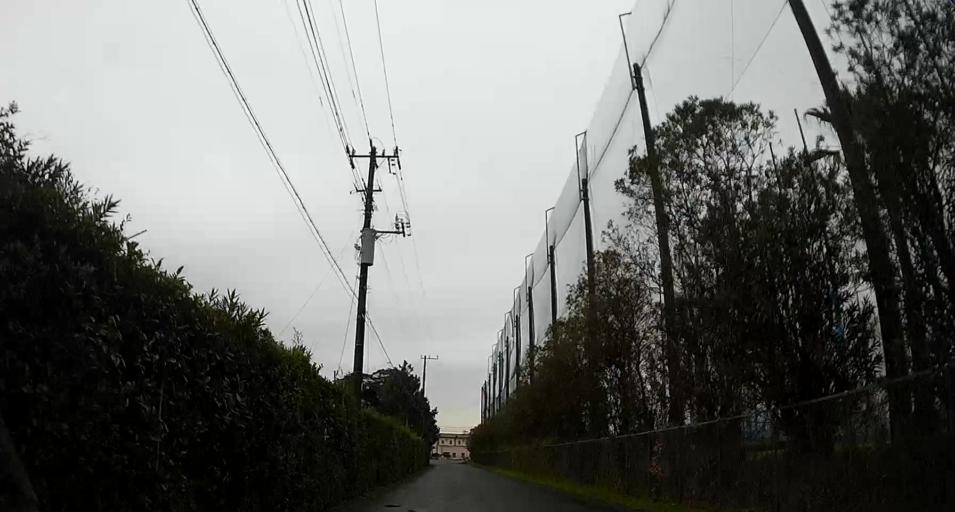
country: JP
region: Chiba
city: Kisarazu
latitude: 35.4073
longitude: 139.9031
